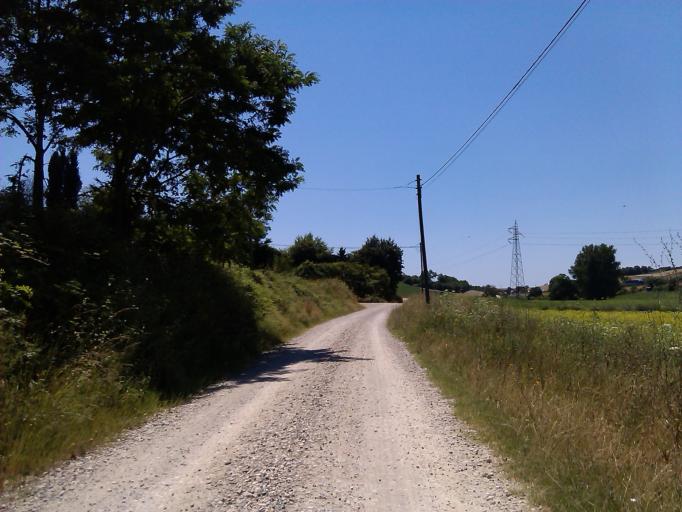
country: IT
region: Umbria
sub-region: Provincia di Terni
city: Ficulle
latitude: 42.8453
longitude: 12.0422
